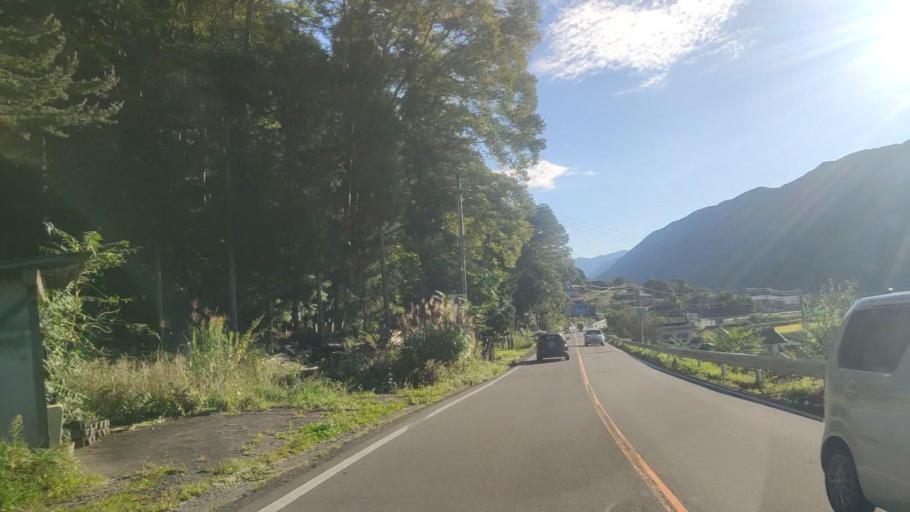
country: JP
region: Nagano
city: Kamimaruko
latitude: 36.2493
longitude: 138.2680
